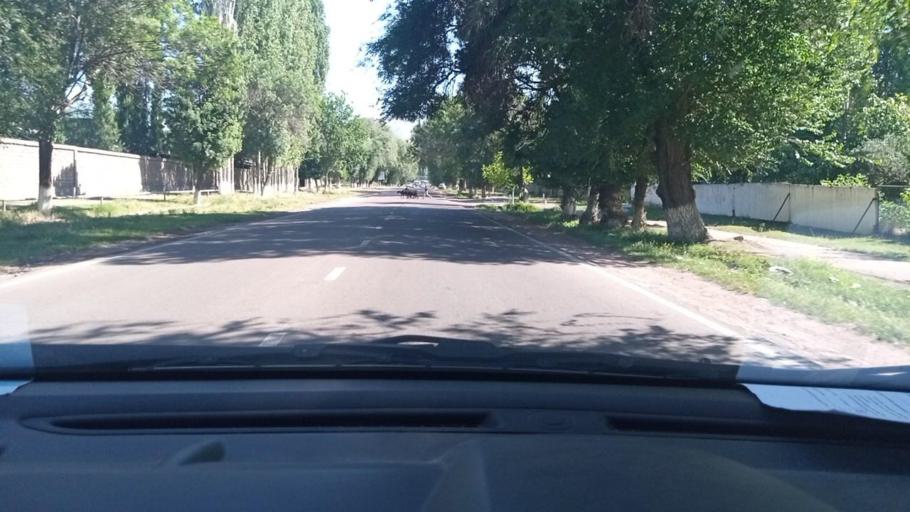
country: UZ
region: Toshkent
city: Angren
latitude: 41.0342
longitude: 70.0924
